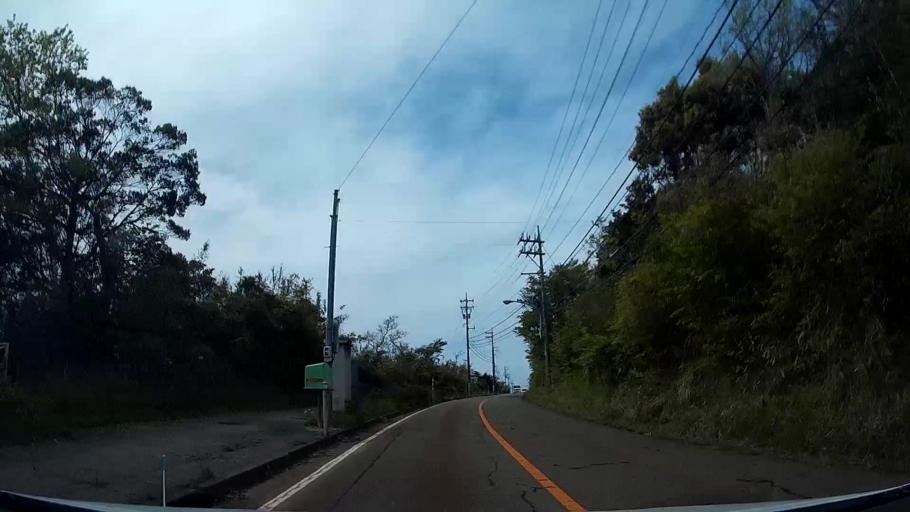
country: JP
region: Ishikawa
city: Hakui
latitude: 37.0081
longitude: 136.7660
